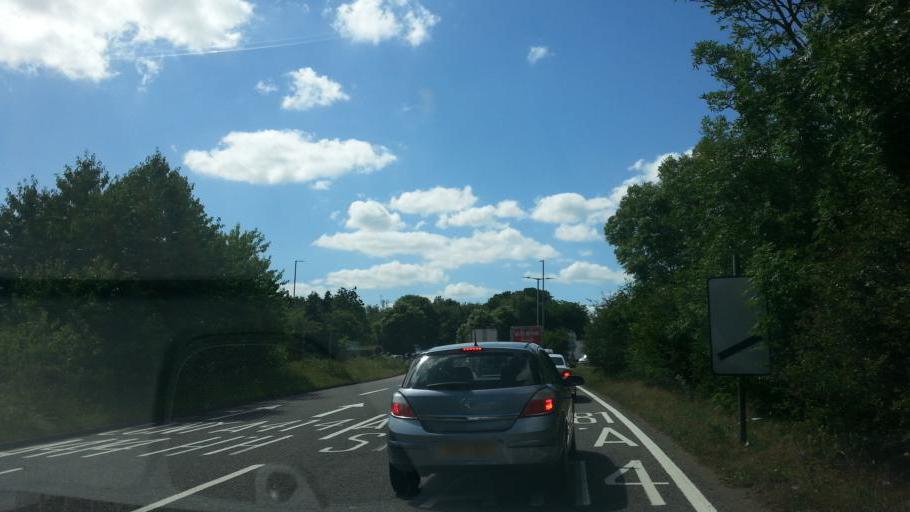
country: GB
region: England
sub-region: Hertfordshire
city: St Albans
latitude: 51.7307
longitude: -0.2993
